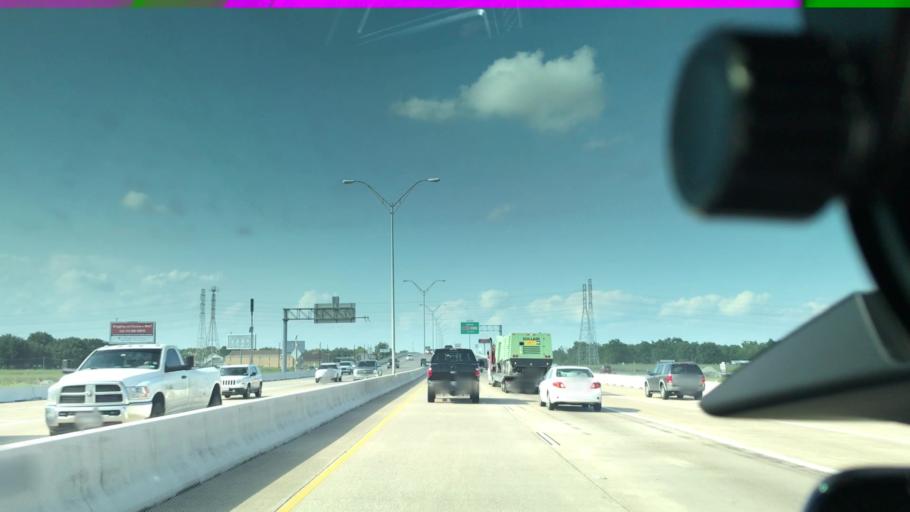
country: US
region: Texas
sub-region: Harris County
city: Deer Park
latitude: 29.6970
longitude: -95.1535
